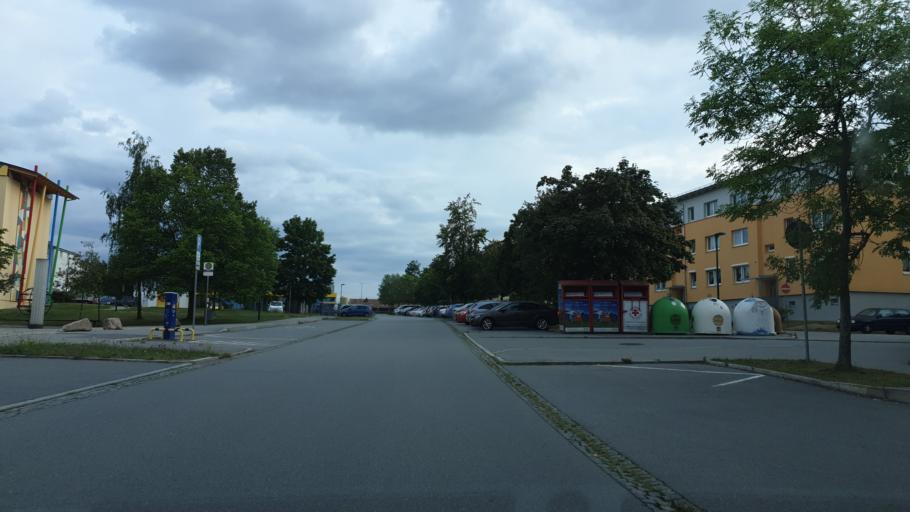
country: DE
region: Saxony
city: Stollberg
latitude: 50.7138
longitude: 12.7680
